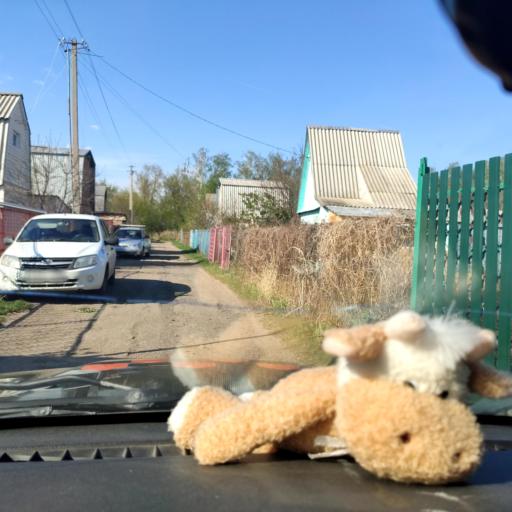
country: RU
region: Samara
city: Tol'yatti
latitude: 53.6021
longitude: 49.2653
